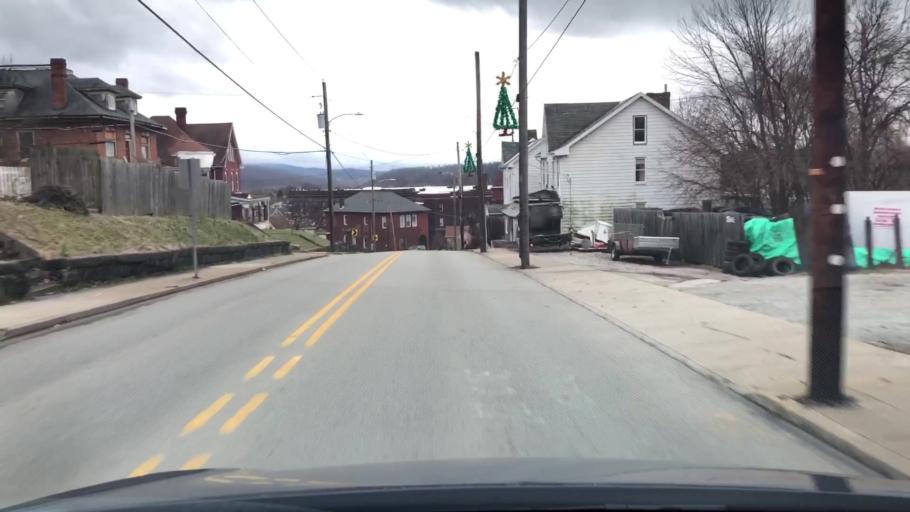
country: US
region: Pennsylvania
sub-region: Fayette County
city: Connellsville
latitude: 40.0191
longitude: -79.5851
